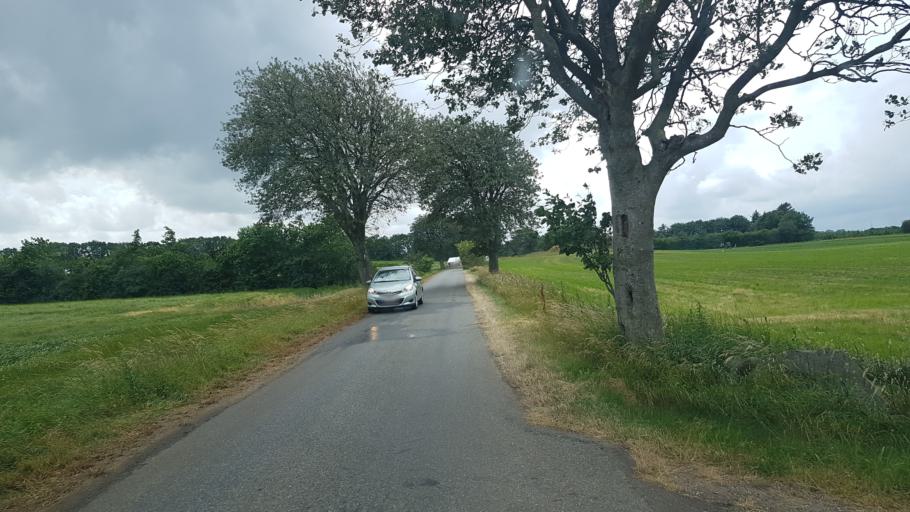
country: DK
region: South Denmark
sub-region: Kolding Kommune
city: Lunderskov
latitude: 55.5018
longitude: 9.3107
